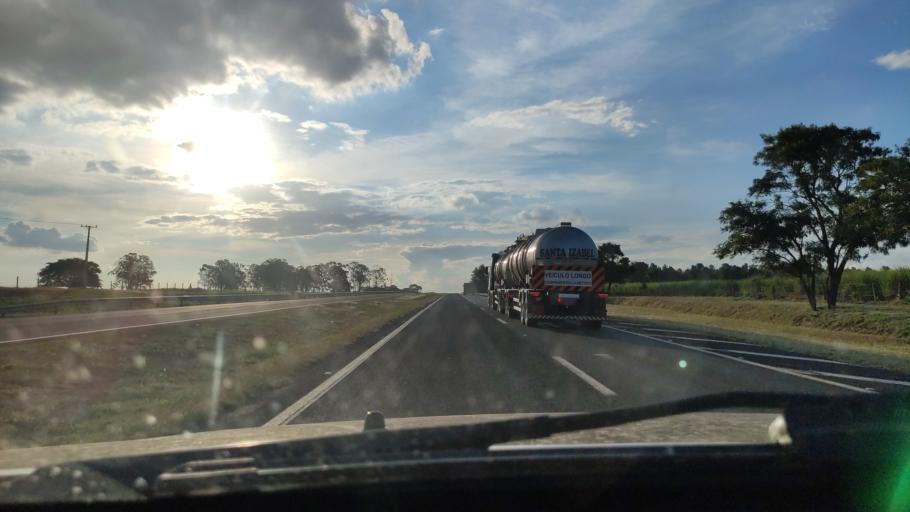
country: BR
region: Sao Paulo
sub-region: Rancharia
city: Rancharia
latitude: -22.4598
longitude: -50.9664
